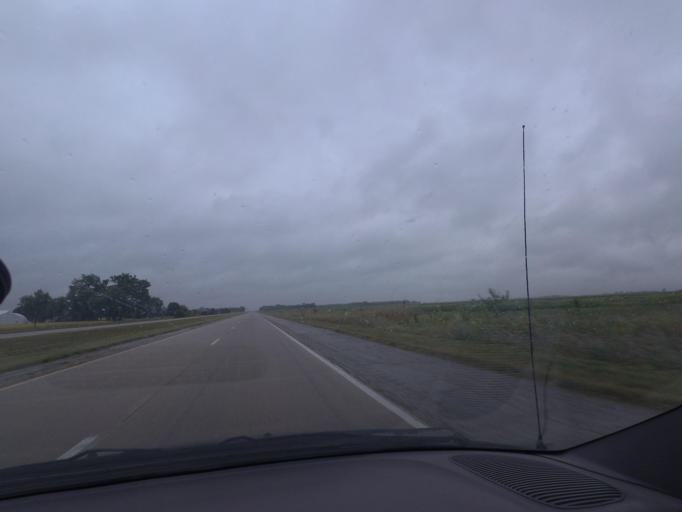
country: US
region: Illinois
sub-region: Adams County
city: Payson
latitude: 39.7426
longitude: -91.2656
